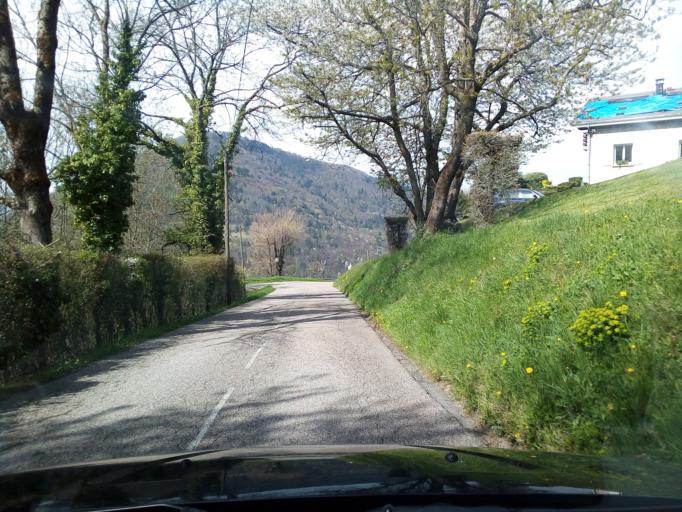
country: FR
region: Rhone-Alpes
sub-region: Departement de l'Isere
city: Herbeys
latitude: 45.1604
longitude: 5.8313
